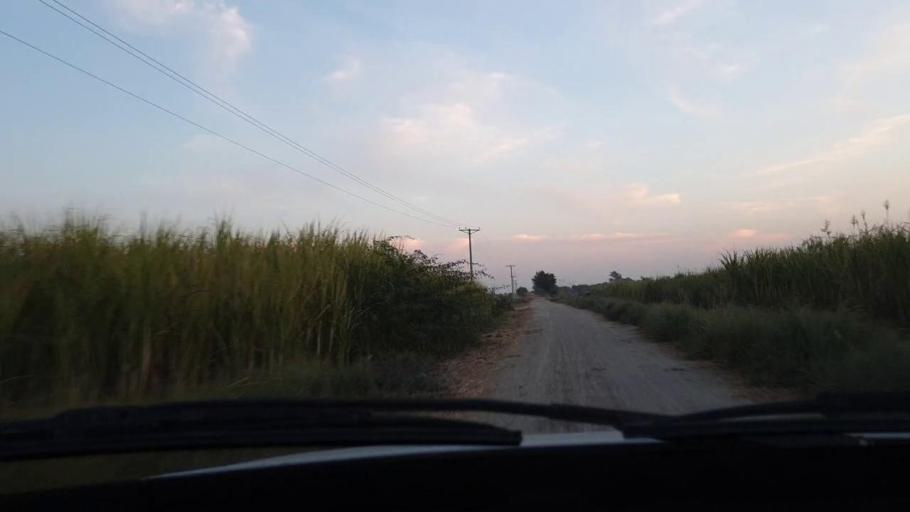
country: PK
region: Sindh
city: Tando Muhammad Khan
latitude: 25.0843
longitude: 68.3975
